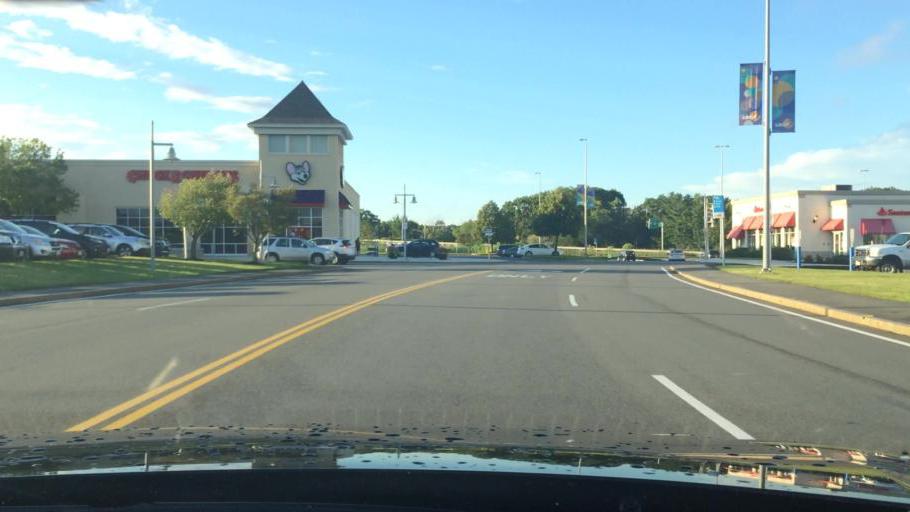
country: US
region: Massachusetts
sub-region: Essex County
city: Lawrence
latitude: 42.7433
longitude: -71.1561
